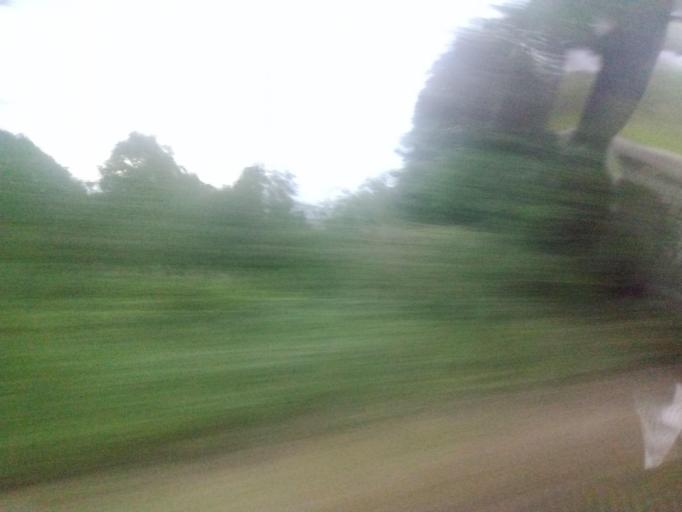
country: IE
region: Leinster
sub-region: Laois
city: Mountmellick
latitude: 53.1290
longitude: -7.3750
